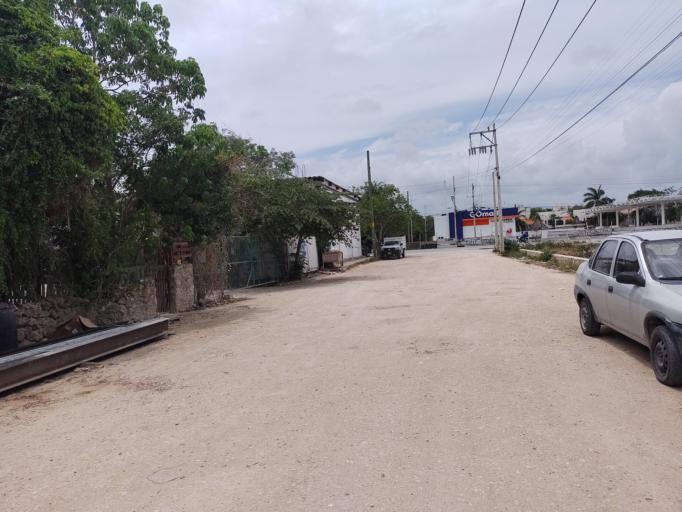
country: MX
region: Quintana Roo
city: Tulum
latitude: 20.2060
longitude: -87.4771
